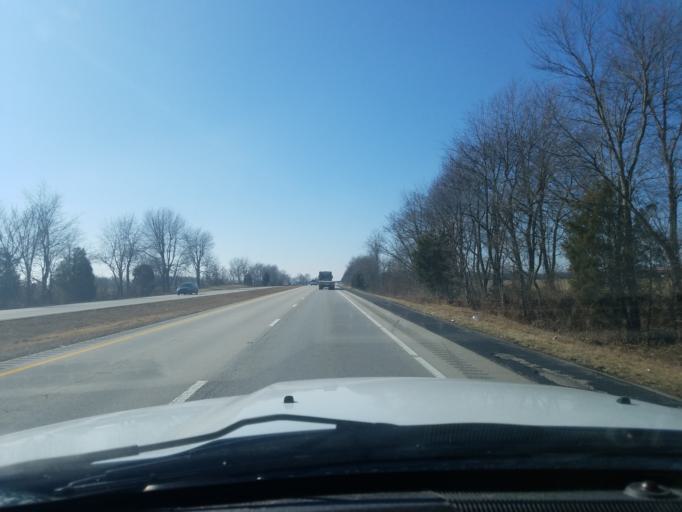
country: US
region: Kentucky
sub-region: Hardin County
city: Elizabethtown
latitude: 37.6246
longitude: -85.9465
